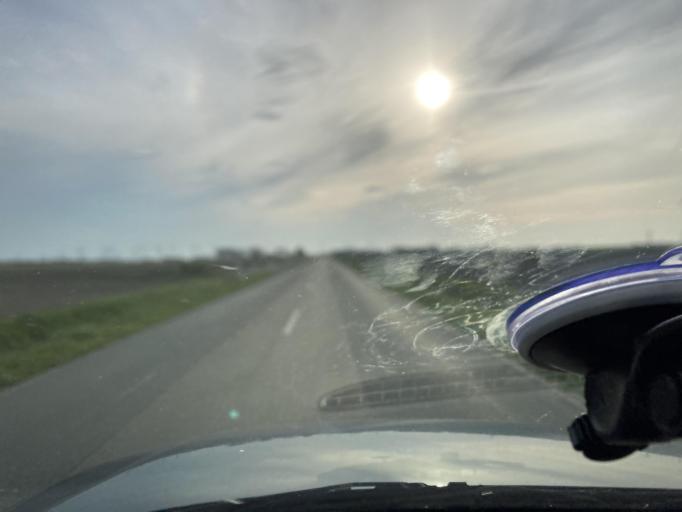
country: DE
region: Schleswig-Holstein
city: Strubbel
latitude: 54.2555
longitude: 8.9609
